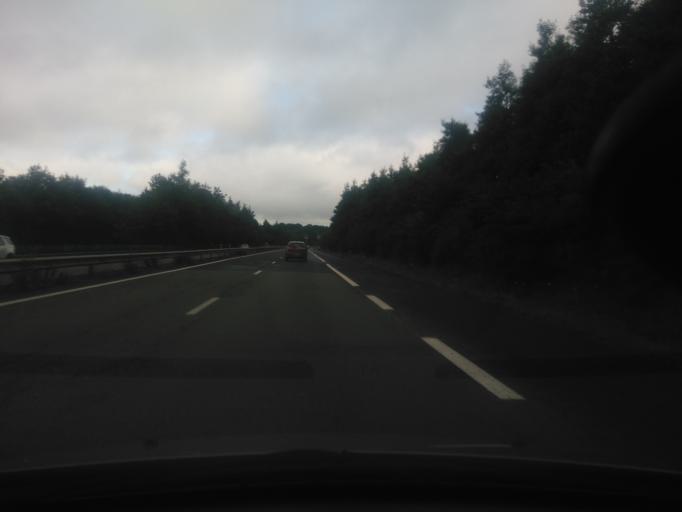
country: FR
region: Brittany
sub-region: Departement d'Ille-et-Vilaine
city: Hede-Bazouges
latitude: 48.2800
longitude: -1.7969
